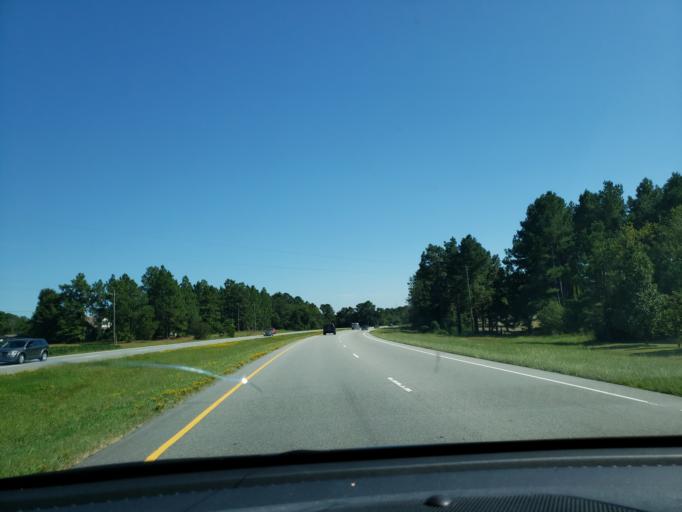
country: US
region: North Carolina
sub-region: Lee County
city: Broadway
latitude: 35.3366
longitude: -79.0967
